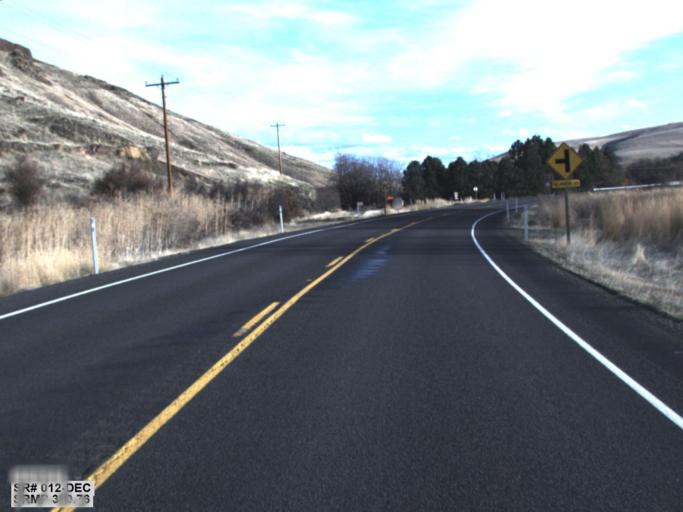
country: US
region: Washington
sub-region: Columbia County
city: Dayton
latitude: 46.4911
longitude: -117.9642
